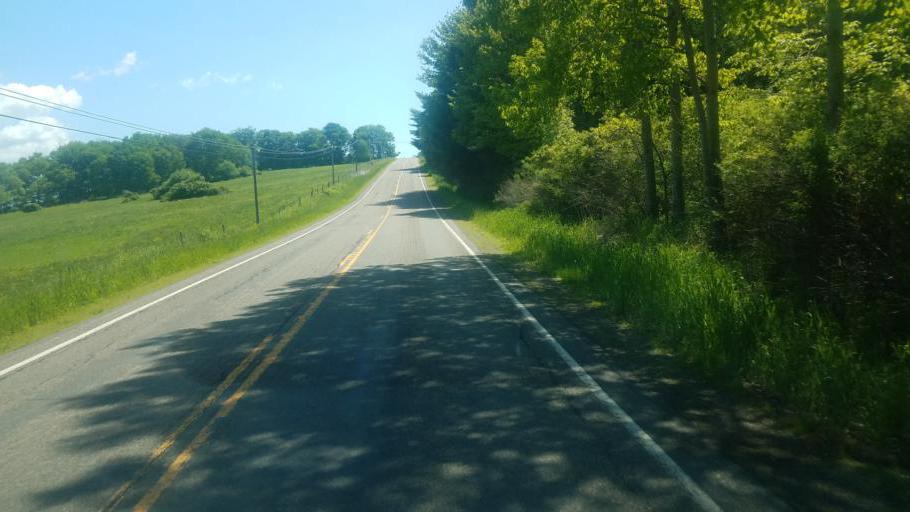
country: US
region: Pennsylvania
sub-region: Tioga County
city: Wellsboro
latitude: 41.7306
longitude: -77.3874
